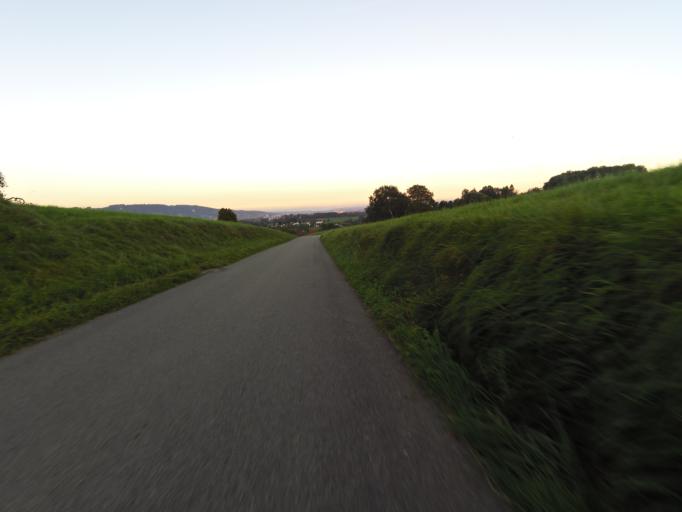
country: CH
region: Thurgau
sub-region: Weinfelden District
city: Maerstetten-Dorf
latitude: 47.5677
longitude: 9.0475
